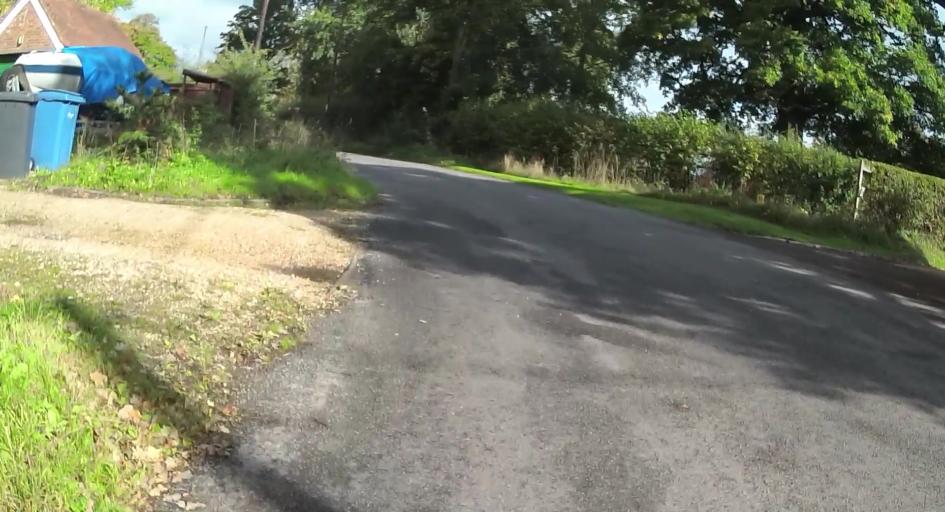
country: GB
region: England
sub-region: Hampshire
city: Odiham
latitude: 51.2765
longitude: -0.9016
